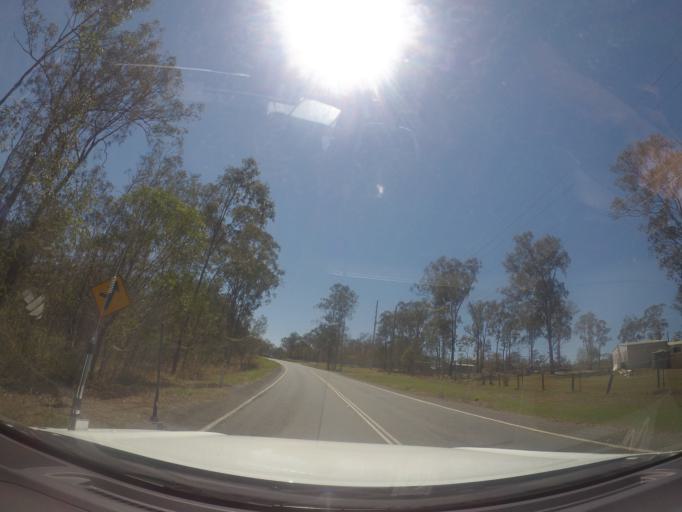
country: AU
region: Queensland
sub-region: Logan
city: North Maclean
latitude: -27.8096
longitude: 153.0427
